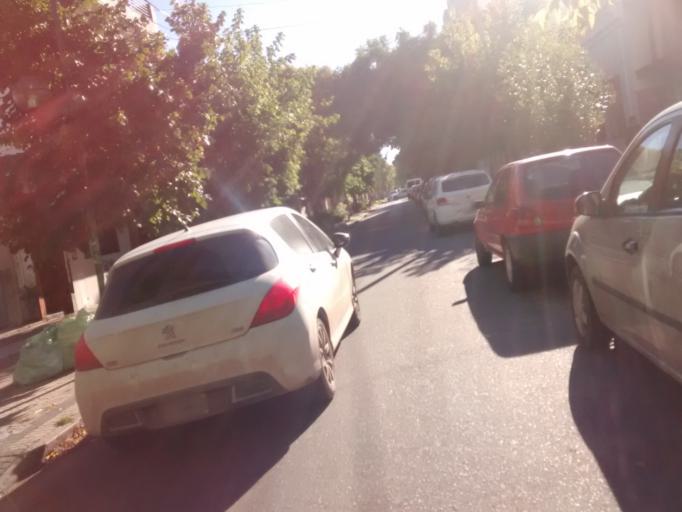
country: AR
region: Buenos Aires
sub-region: Partido de La Plata
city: La Plata
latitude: -34.9231
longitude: -57.9379
